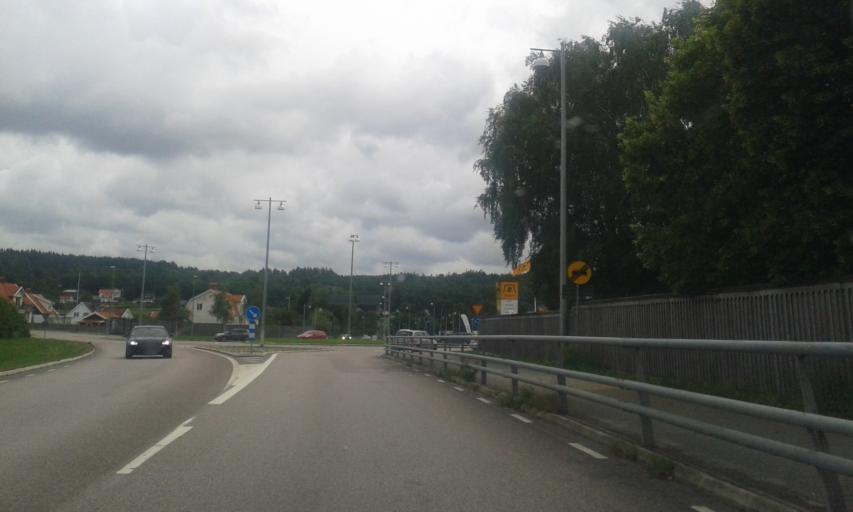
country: SE
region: Vaestra Goetaland
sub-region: Kungalvs Kommun
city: Kungalv
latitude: 57.8655
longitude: 11.9238
